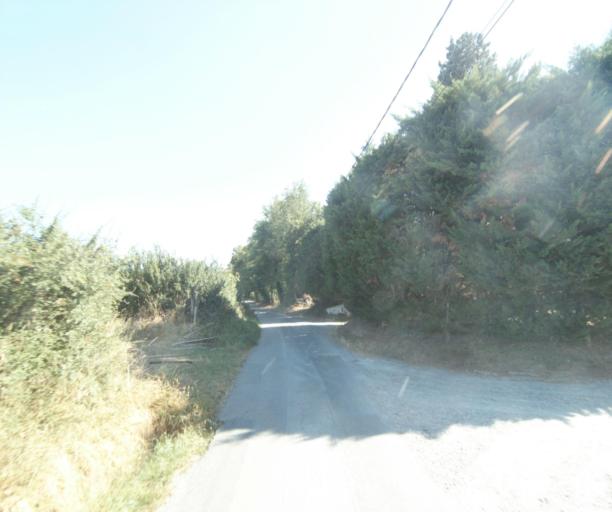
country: FR
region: Rhone-Alpes
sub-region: Departement du Rhone
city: La Tour-de-Salvagny
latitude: 45.8306
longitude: 4.7231
